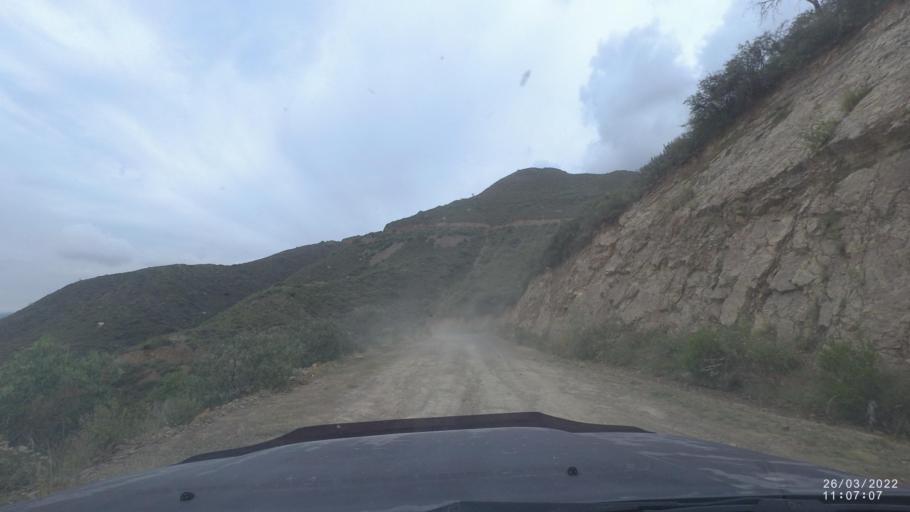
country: BO
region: Cochabamba
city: Tarata
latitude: -17.5343
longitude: -66.0185
